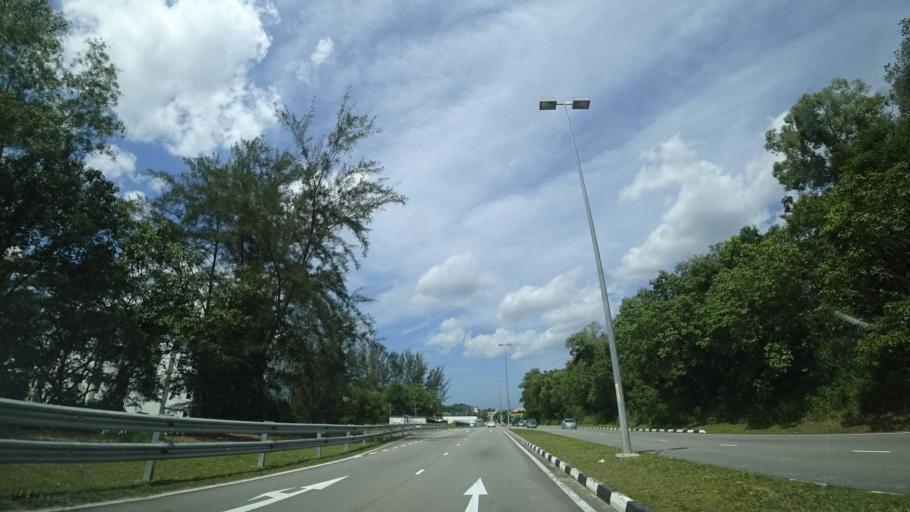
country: BN
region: Brunei and Muara
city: Bandar Seri Begawan
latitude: 4.9021
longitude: 114.9099
